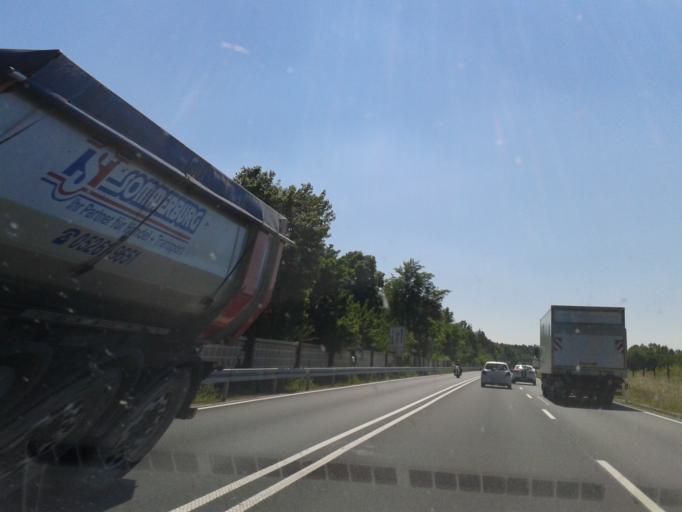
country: DE
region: North Rhine-Westphalia
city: Bad Lippspringe
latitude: 51.7922
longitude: 8.7995
